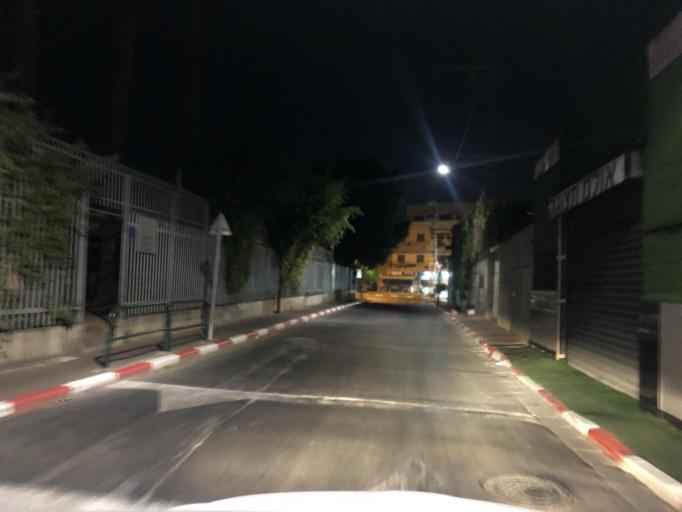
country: IL
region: Tel Aviv
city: Azor
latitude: 32.0469
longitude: 34.7945
